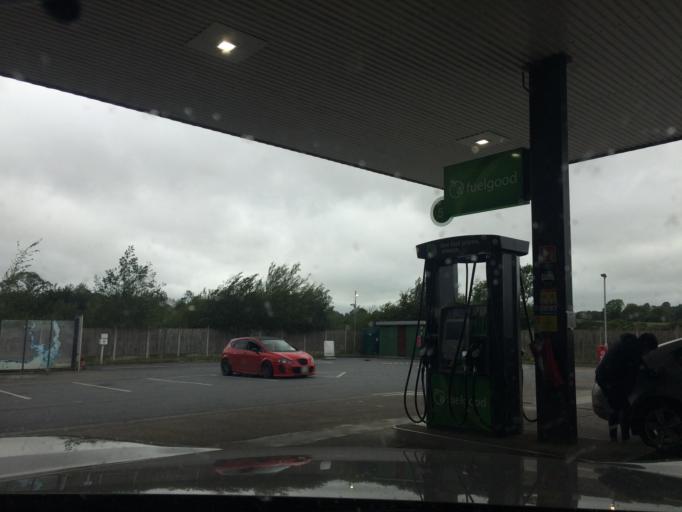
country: IE
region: Munster
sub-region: South Tipperary
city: Cluain Meala
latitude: 52.3454
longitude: -7.7186
